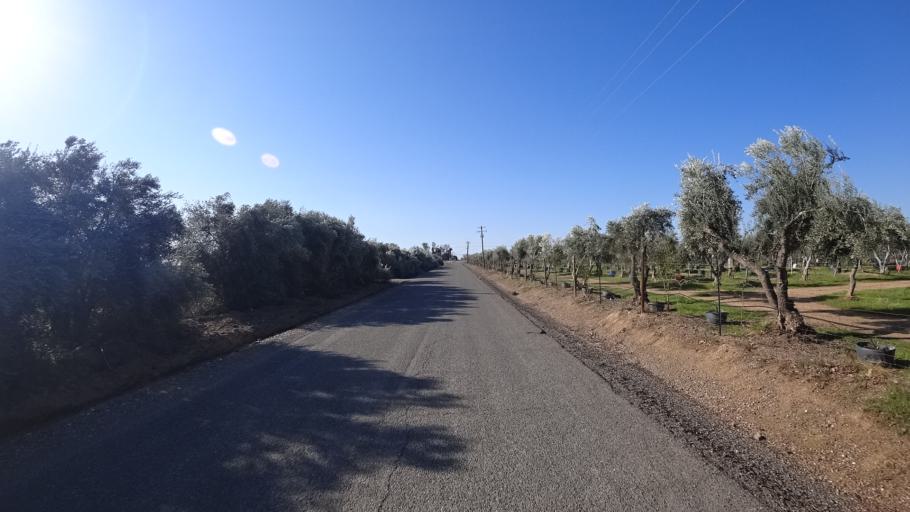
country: US
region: California
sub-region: Glenn County
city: Orland
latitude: 39.7704
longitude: -122.1227
